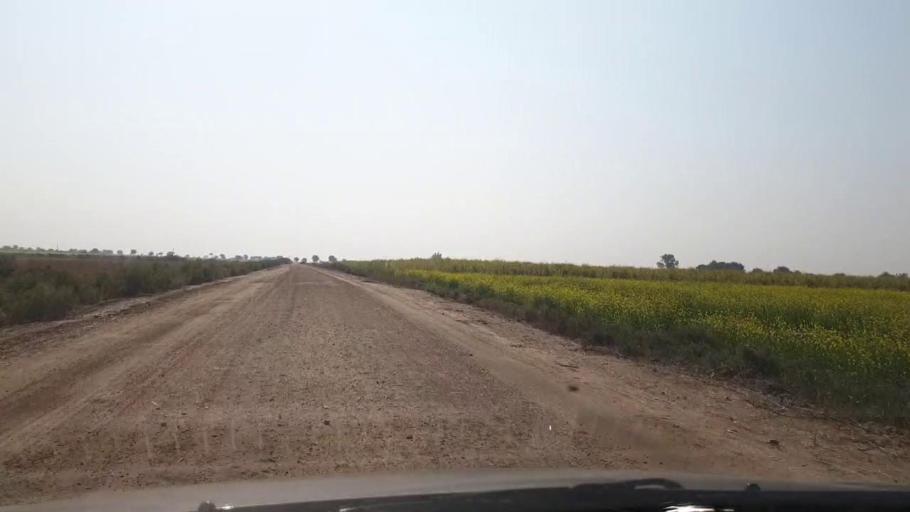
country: PK
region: Sindh
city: Jhol
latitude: 25.8675
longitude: 68.9980
